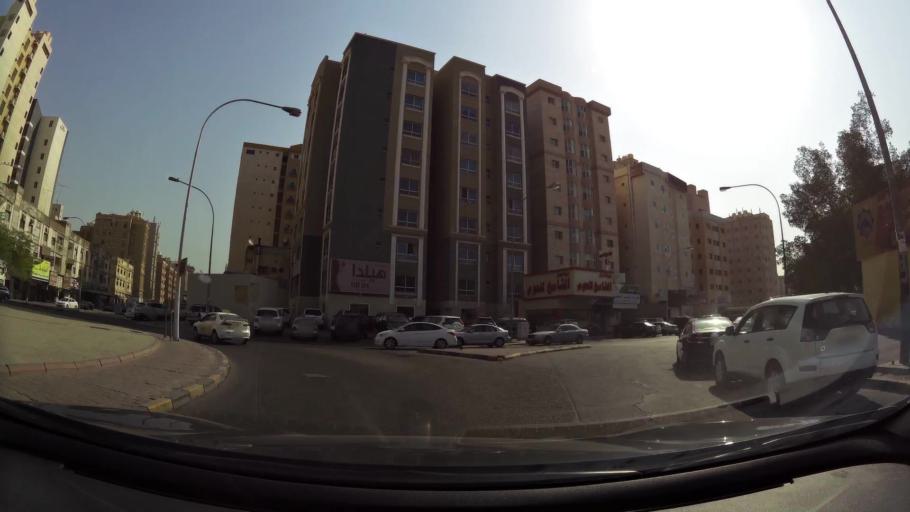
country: KW
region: Muhafazat Hawalli
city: Hawalli
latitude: 29.3252
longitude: 48.0139
